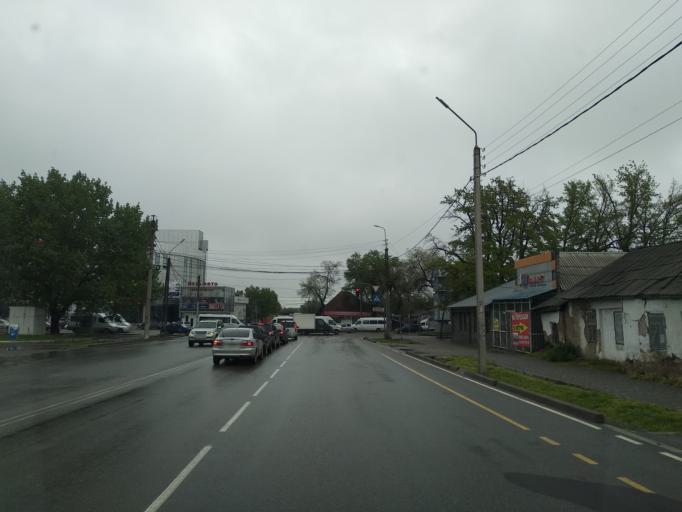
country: KG
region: Chuy
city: Bishkek
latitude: 42.8844
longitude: 74.6171
